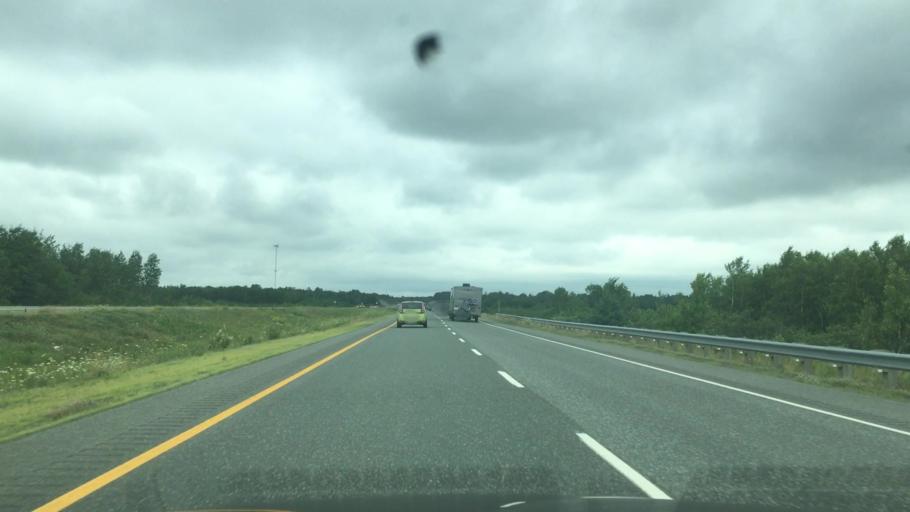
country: CA
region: Nova Scotia
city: Truro
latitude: 45.3942
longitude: -63.4126
